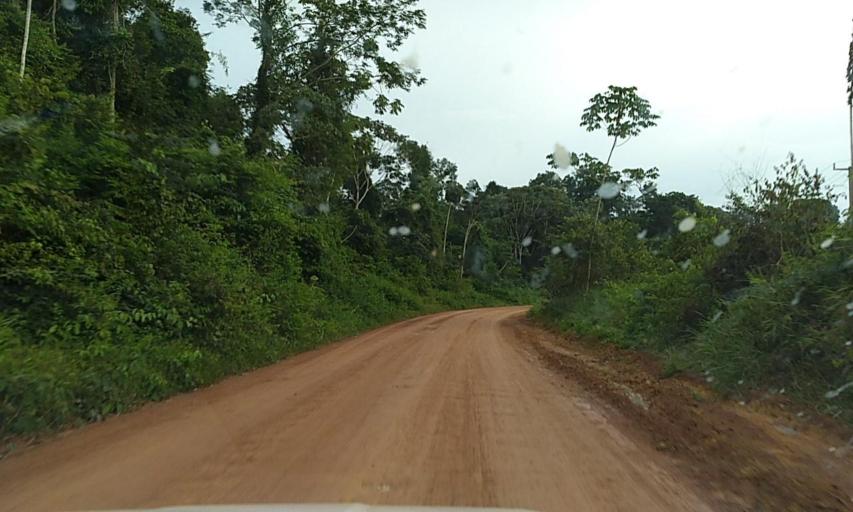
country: BR
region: Para
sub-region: Senador Jose Porfirio
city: Senador Jose Porfirio
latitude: -2.7125
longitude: -51.8043
